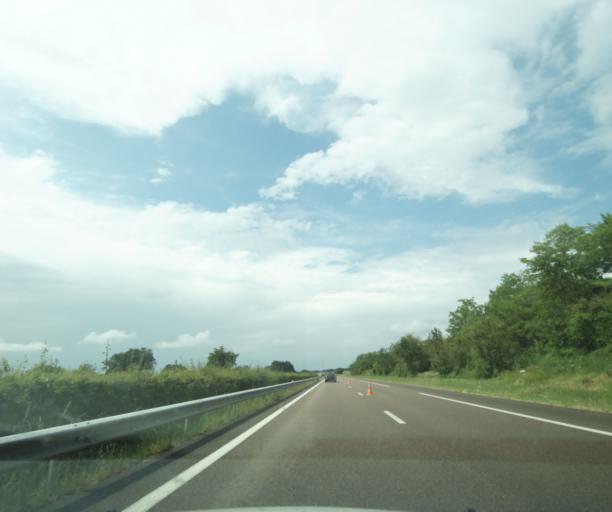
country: FR
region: Auvergne
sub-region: Departement de l'Allier
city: Estivareilles
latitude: 46.4689
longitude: 2.6779
